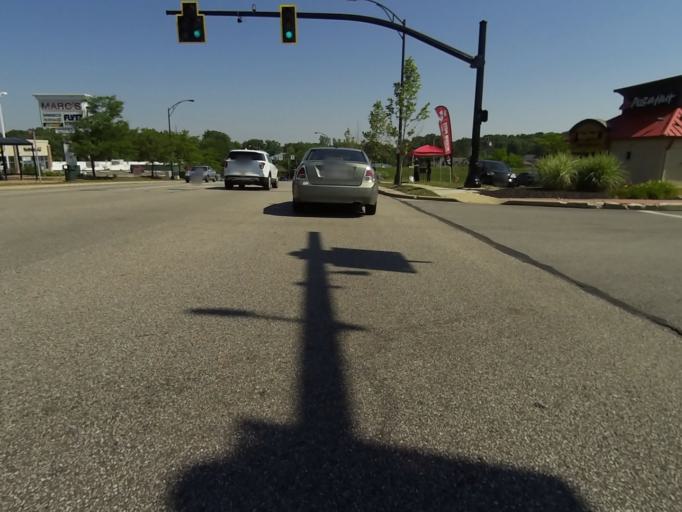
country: US
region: Ohio
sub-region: Summit County
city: Cuyahoga Falls
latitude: 41.1508
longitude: -81.5084
